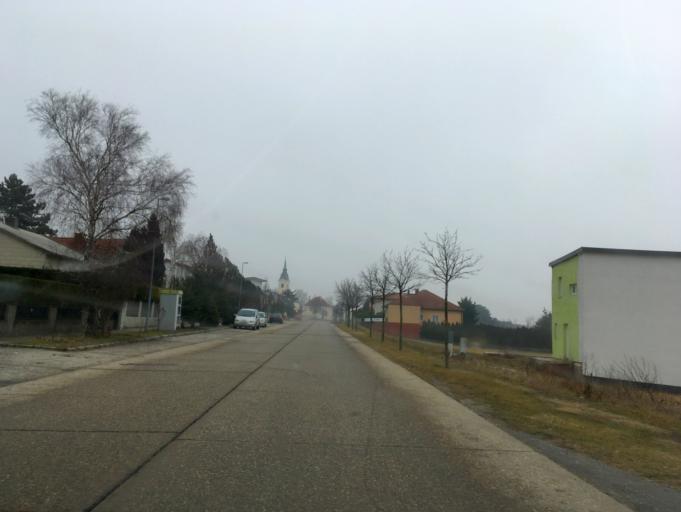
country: AT
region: Lower Austria
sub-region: Politischer Bezirk Bruck an der Leitha
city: Trautmannsdorf an der Leitha
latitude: 48.0566
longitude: 16.6333
